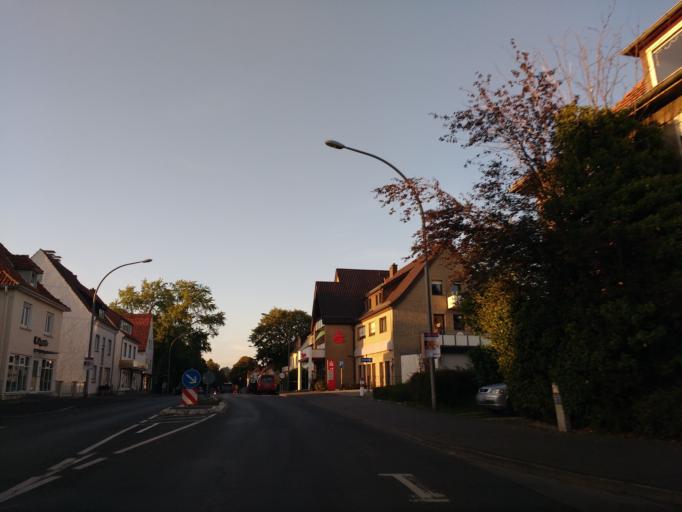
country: DE
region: North Rhine-Westphalia
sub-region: Regierungsbezirk Detmold
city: Detmold
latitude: 51.9471
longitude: 8.8796
